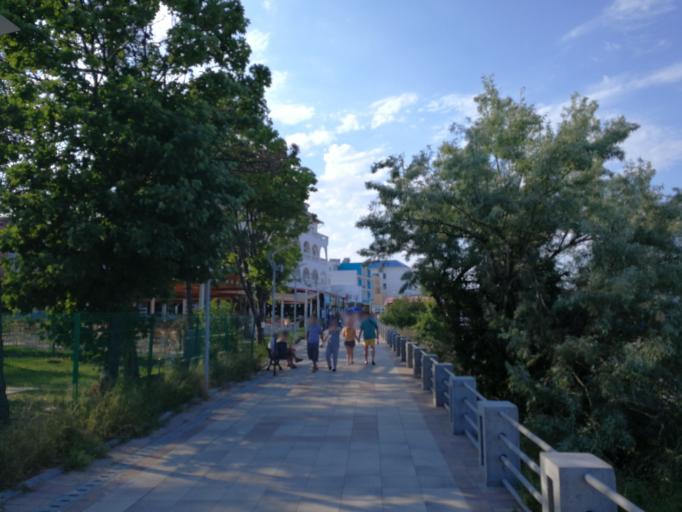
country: RO
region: Constanta
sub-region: Oras Eforie
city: Eforie Nord
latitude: 44.0680
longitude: 28.6389
